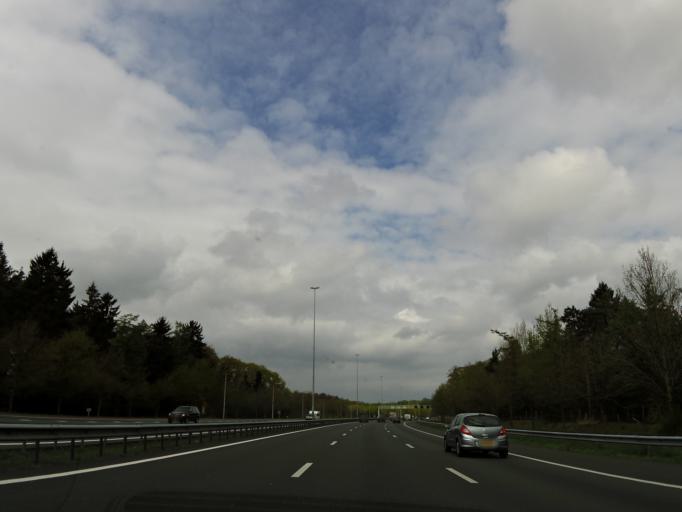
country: NL
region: North Brabant
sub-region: Gemeente Boxtel
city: Boxtel
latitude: 51.6107
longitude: 5.3216
